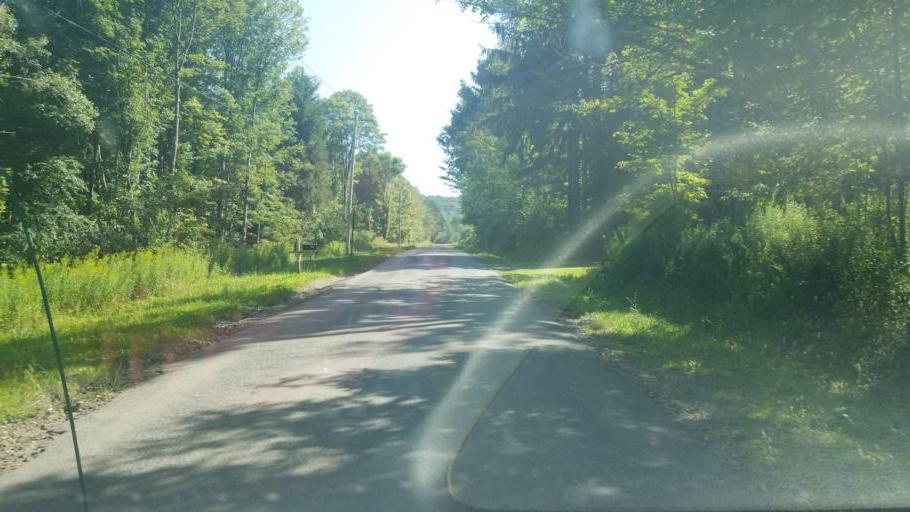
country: US
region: New York
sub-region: Allegany County
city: Bolivar
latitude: 42.0731
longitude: -78.0603
